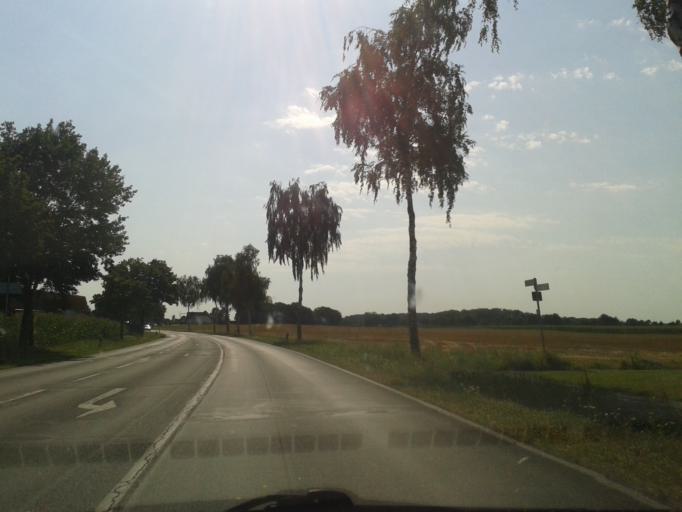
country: DE
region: North Rhine-Westphalia
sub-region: Regierungsbezirk Detmold
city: Delbruck
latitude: 51.7761
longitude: 8.5891
